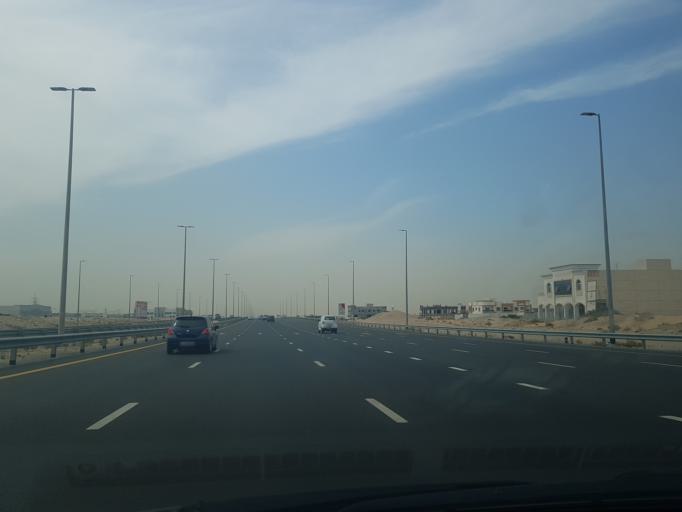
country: AE
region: Ash Shariqah
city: Sharjah
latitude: 25.2432
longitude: 55.5532
